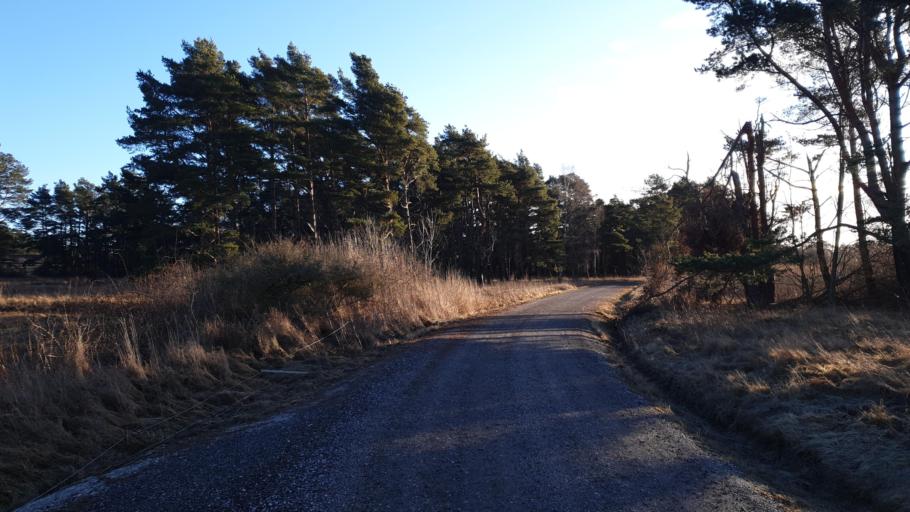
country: SE
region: Gotland
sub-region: Gotland
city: Slite
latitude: 57.3742
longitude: 18.8032
